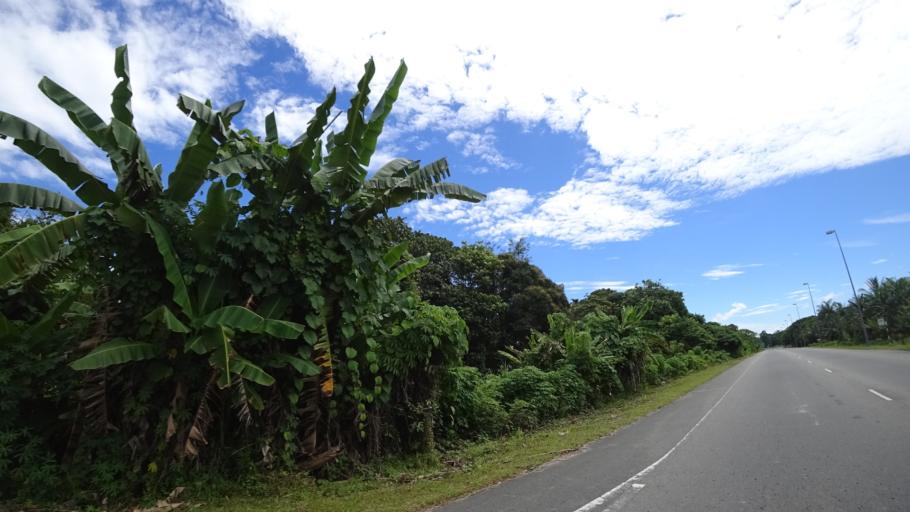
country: BN
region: Tutong
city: Tutong
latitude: 4.7688
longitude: 114.8193
